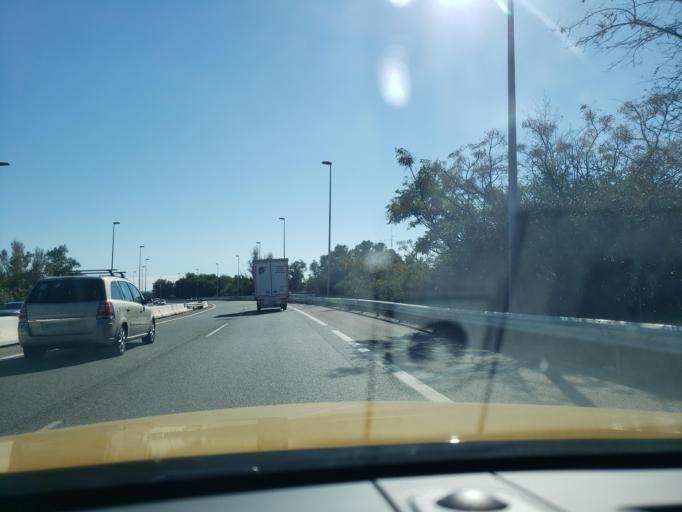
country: ES
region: Andalusia
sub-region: Provincia de Malaga
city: Marbella
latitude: 36.5117
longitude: -4.8634
